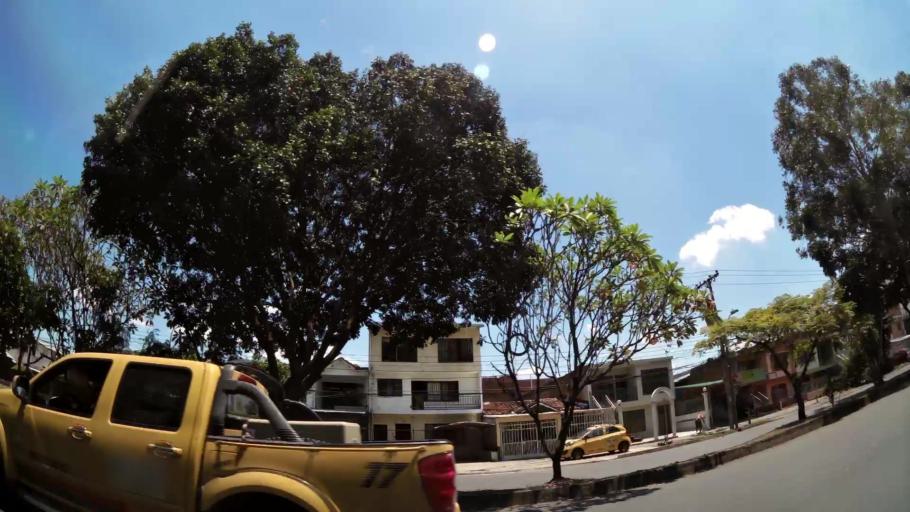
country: CO
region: Valle del Cauca
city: Cali
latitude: 3.4401
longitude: -76.4925
